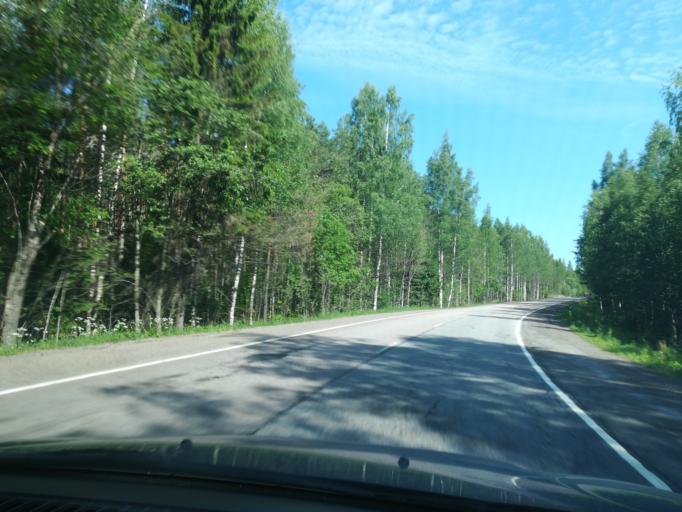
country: RU
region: Leningrad
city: Lesogorskiy
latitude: 60.9321
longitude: 28.8893
